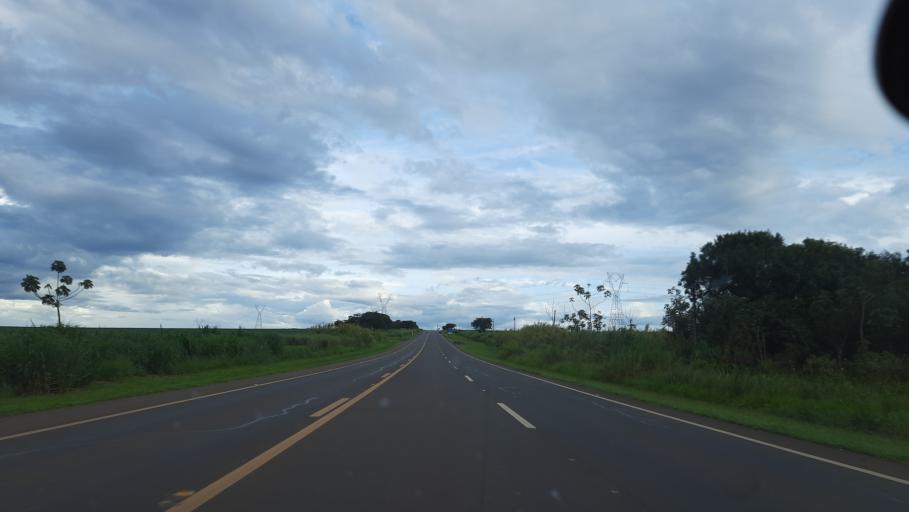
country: BR
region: Sao Paulo
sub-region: Casa Branca
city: Casa Branca
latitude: -21.8088
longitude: -46.9980
